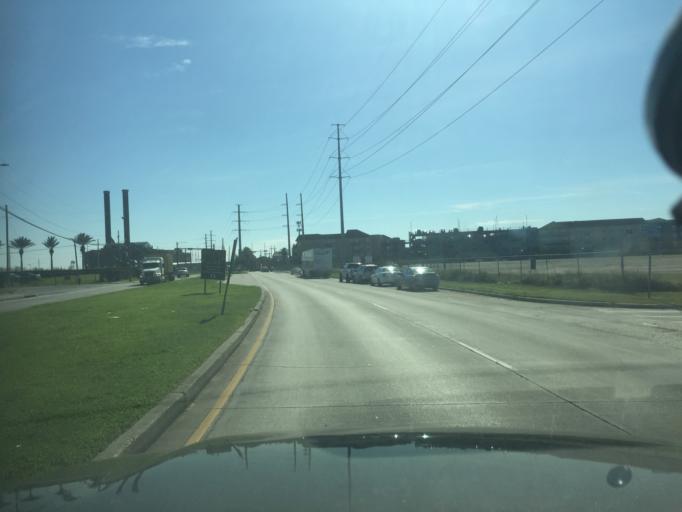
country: US
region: Louisiana
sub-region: Orleans Parish
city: New Orleans
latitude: 29.9364
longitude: -90.0666
